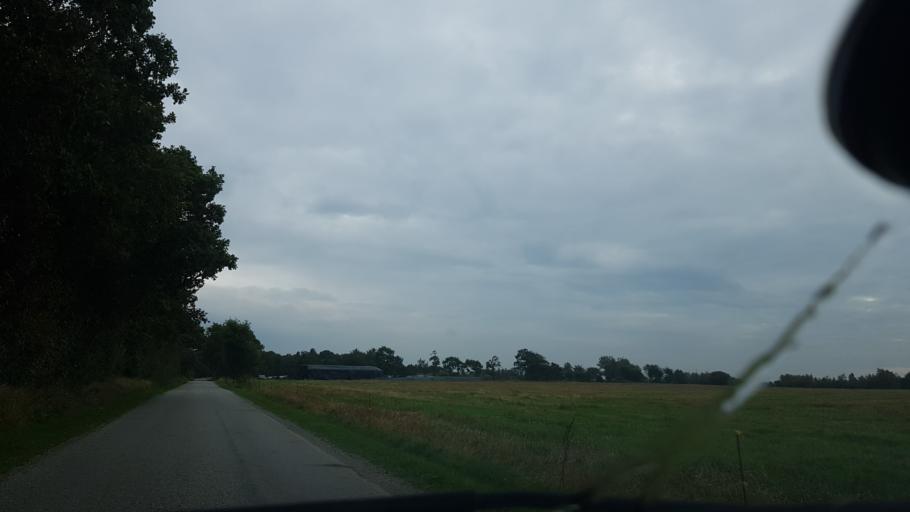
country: DK
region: South Denmark
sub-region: Vejle Kommune
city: Egtved
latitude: 55.5897
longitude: 9.2076
